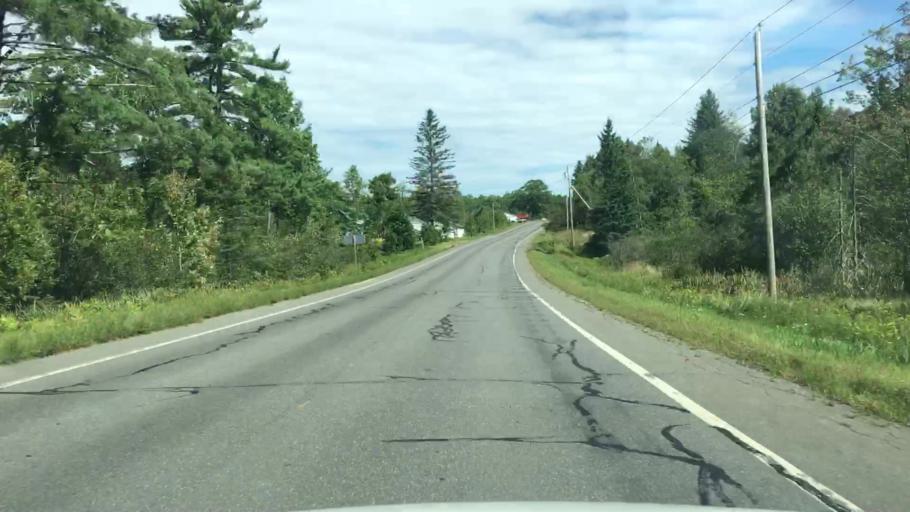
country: US
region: Maine
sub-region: Penobscot County
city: Garland
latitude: 45.0798
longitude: -69.2301
